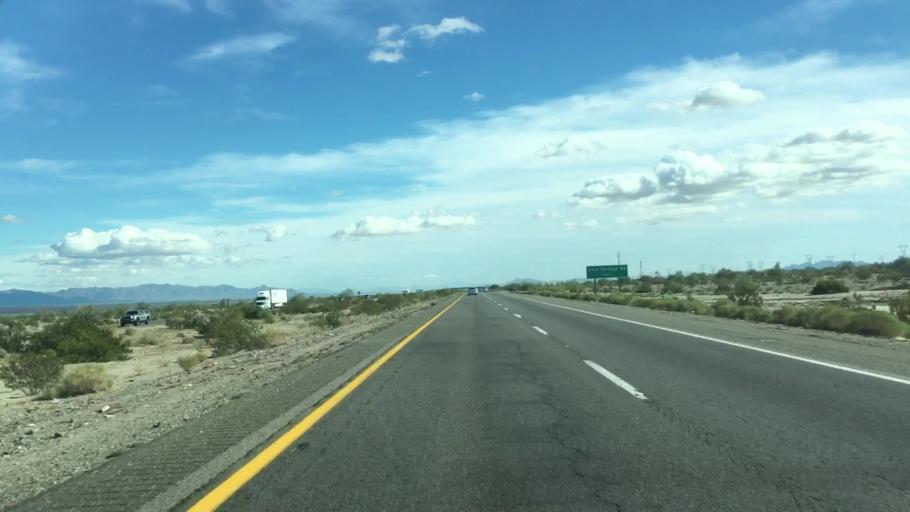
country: US
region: California
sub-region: Imperial County
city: Niland
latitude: 33.6878
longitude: -115.2620
